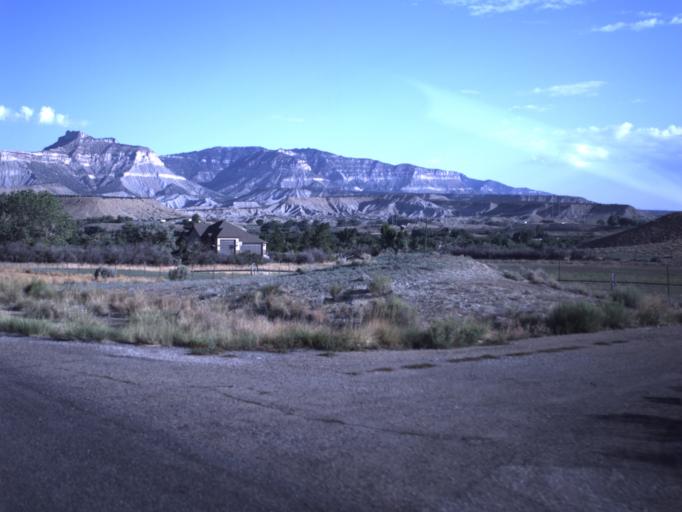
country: US
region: Utah
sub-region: Emery County
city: Huntington
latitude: 39.3416
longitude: -110.9808
